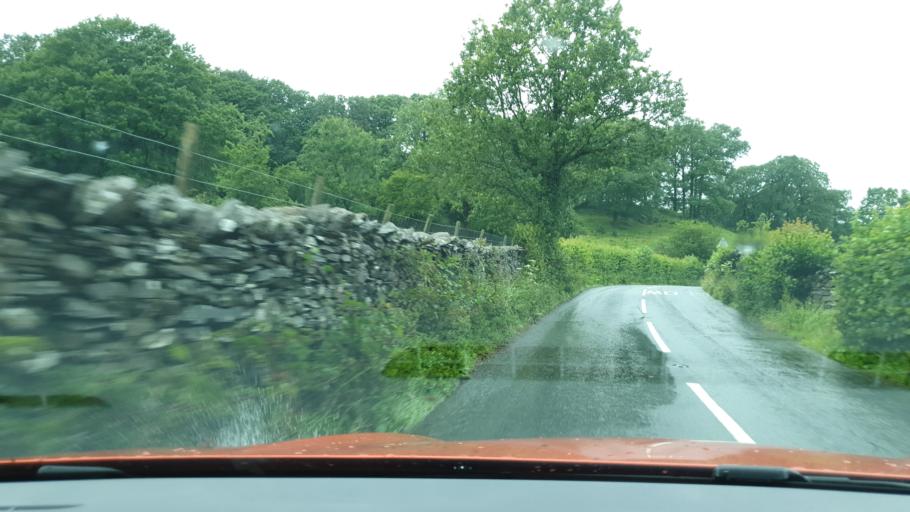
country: GB
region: England
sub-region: Cumbria
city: Ulverston
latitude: 54.2904
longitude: -3.0938
